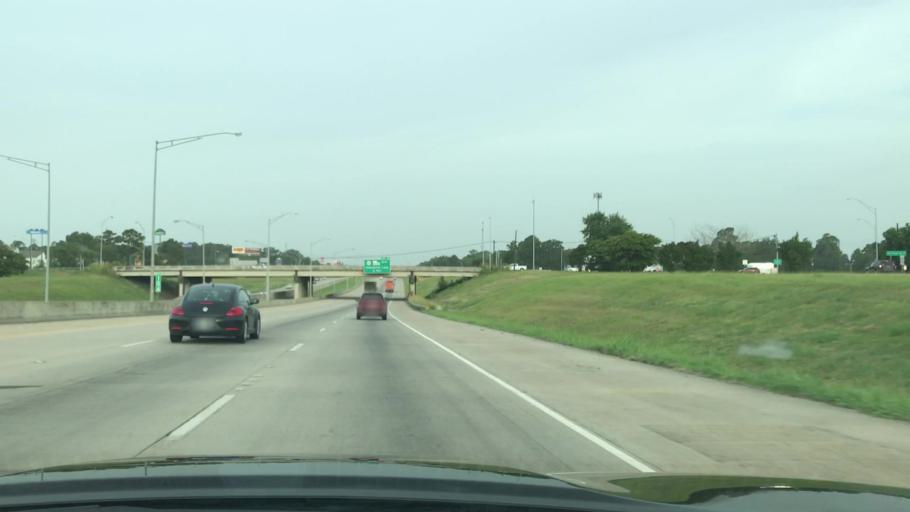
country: US
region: Louisiana
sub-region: Caddo Parish
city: Greenwood
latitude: 32.4510
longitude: -93.8634
